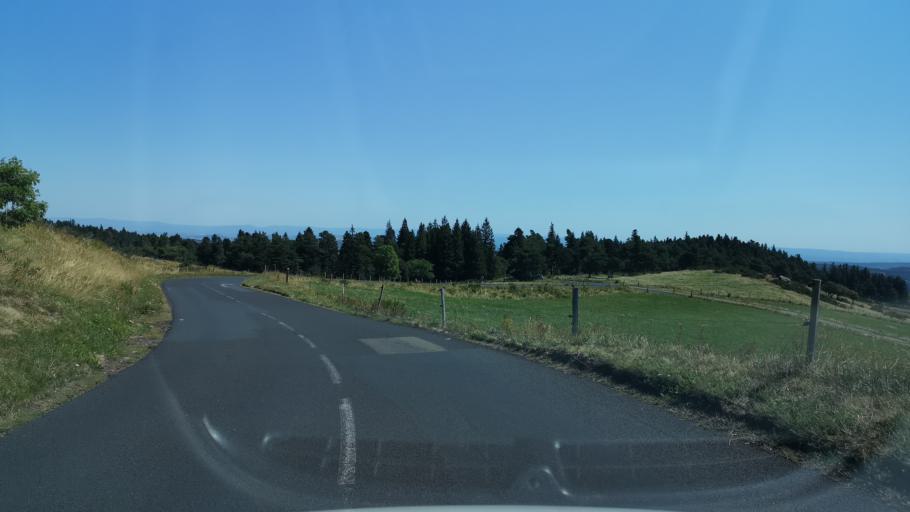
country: FR
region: Auvergne
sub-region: Departement du Puy-de-Dome
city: Mont-Dore
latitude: 45.5877
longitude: 2.8792
